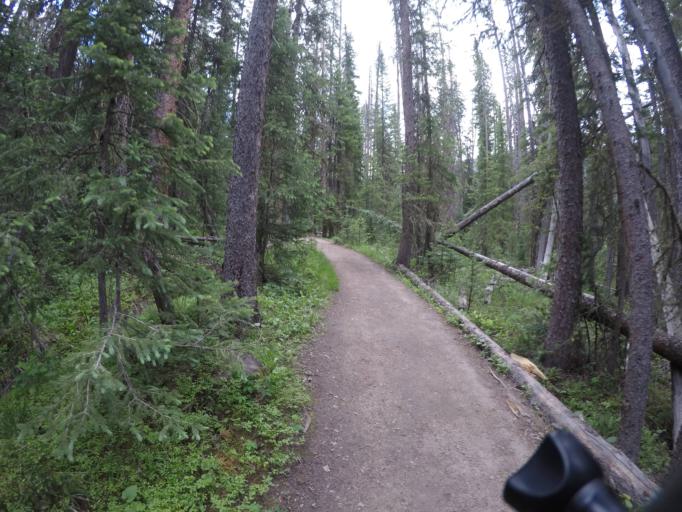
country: US
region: Colorado
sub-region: Grand County
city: Granby
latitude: 40.3098
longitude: -105.8225
